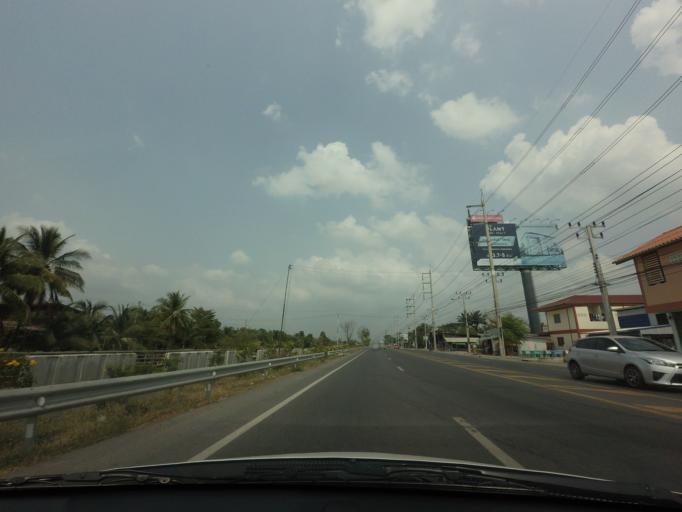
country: TH
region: Pathum Thani
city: Thanyaburi
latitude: 14.0507
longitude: 100.7101
